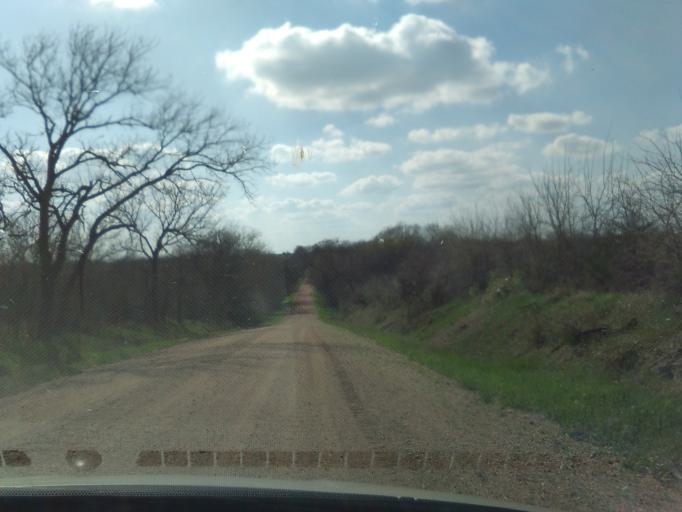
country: US
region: Nebraska
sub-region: Webster County
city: Red Cloud
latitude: 40.0025
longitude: -98.3442
